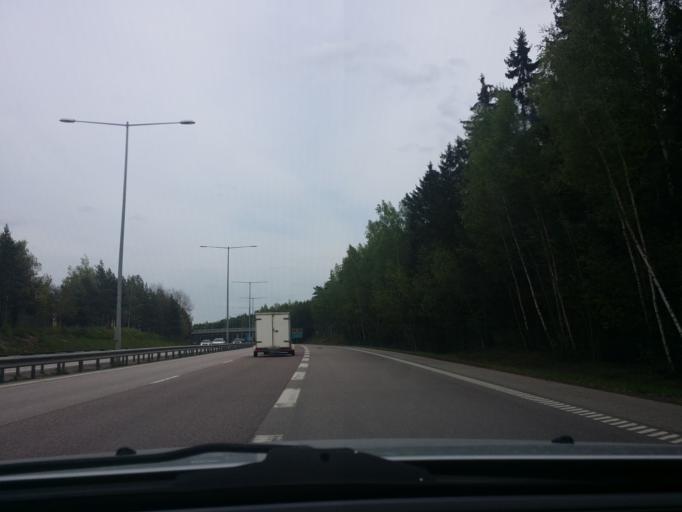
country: SE
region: Vaestmanland
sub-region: Vasteras
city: Vasteras
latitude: 59.6078
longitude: 16.6055
